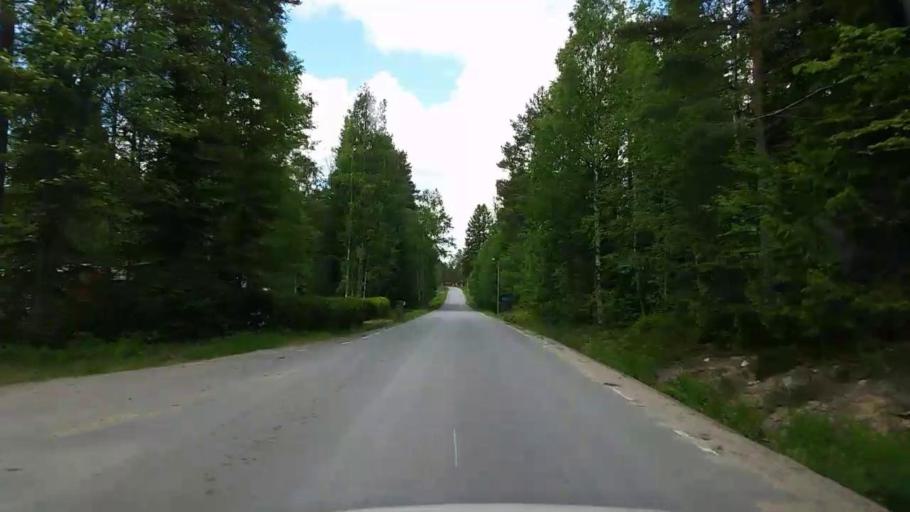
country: SE
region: Gaevleborg
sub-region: Bollnas Kommun
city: Vittsjo
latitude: 61.0954
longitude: 16.1671
